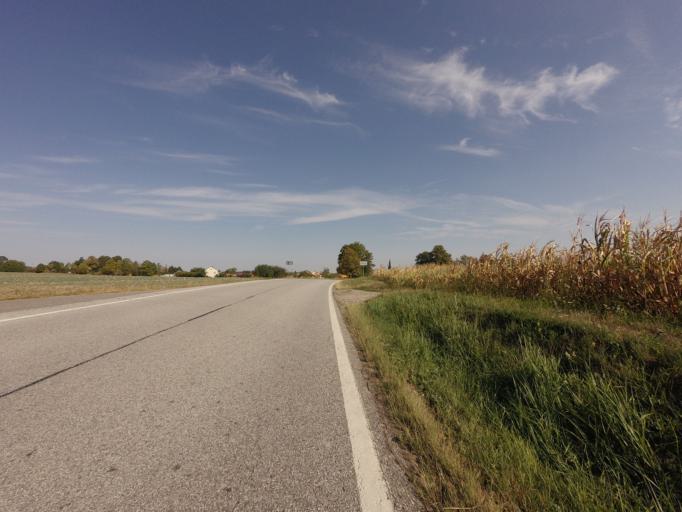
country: CZ
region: Jihocesky
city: Tyn nad Vltavou
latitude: 49.2912
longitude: 14.3910
